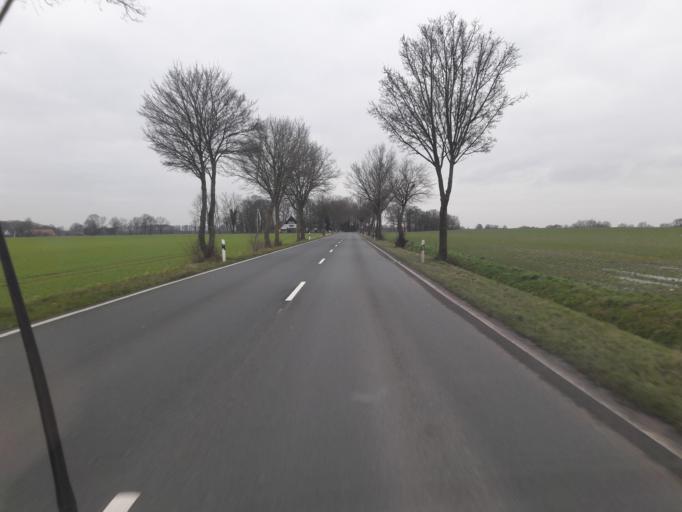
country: DE
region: Lower Saxony
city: Warmsen
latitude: 52.3641
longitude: 8.8491
